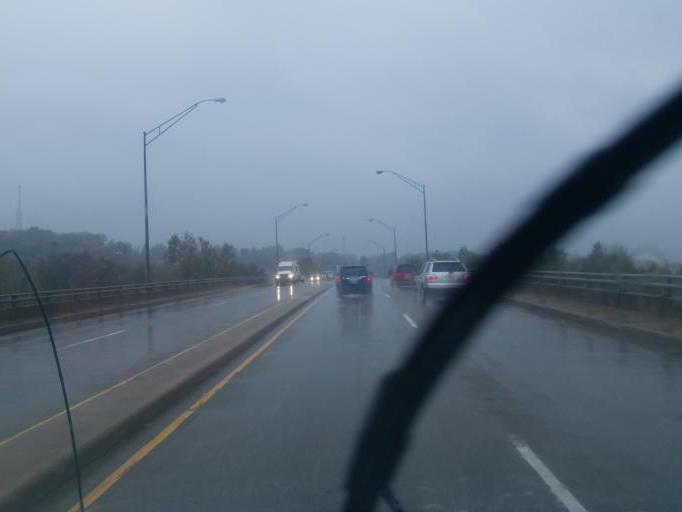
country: US
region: Ohio
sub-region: Muskingum County
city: Zanesville
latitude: 39.9506
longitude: -82.0022
